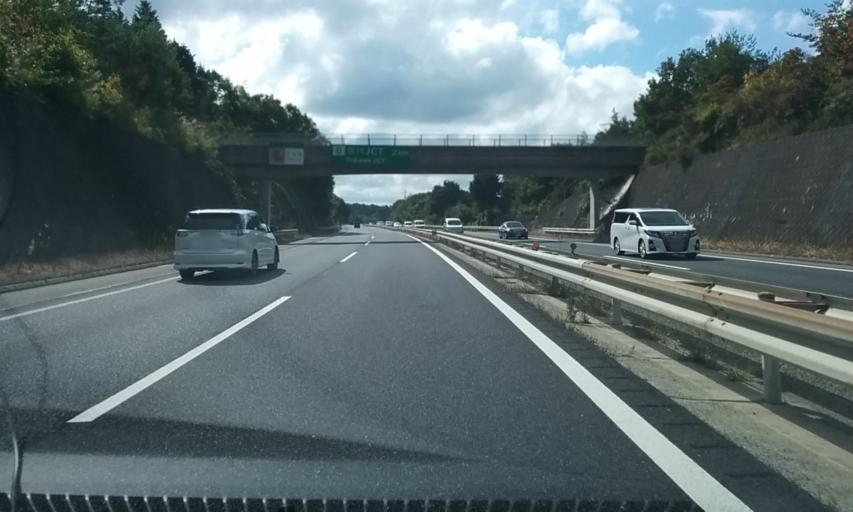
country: JP
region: Hyogo
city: Sandacho
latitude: 34.9127
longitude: 135.1545
